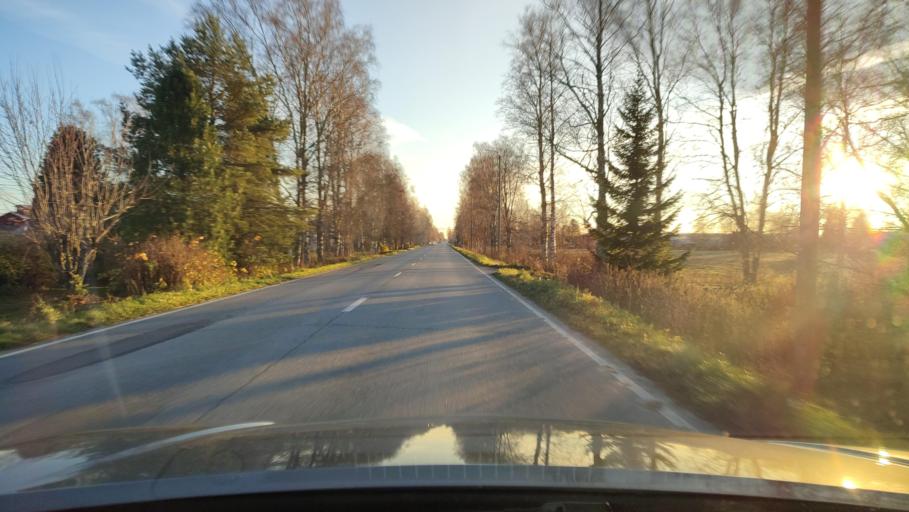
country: FI
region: Ostrobothnia
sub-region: Sydosterbotten
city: Naerpes
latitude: 62.5522
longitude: 21.4041
